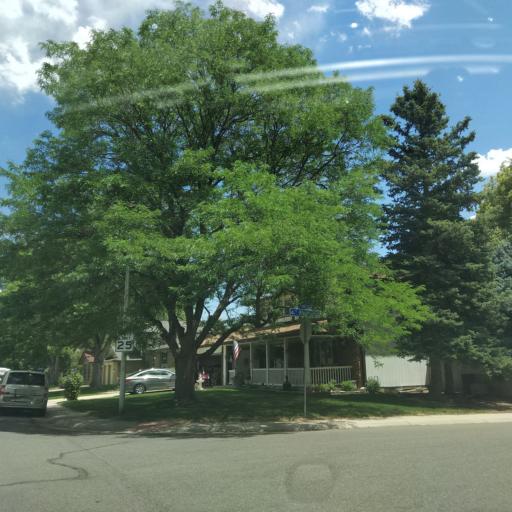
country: US
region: Colorado
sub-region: Jefferson County
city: Lakewood
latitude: 39.6864
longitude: -105.1115
